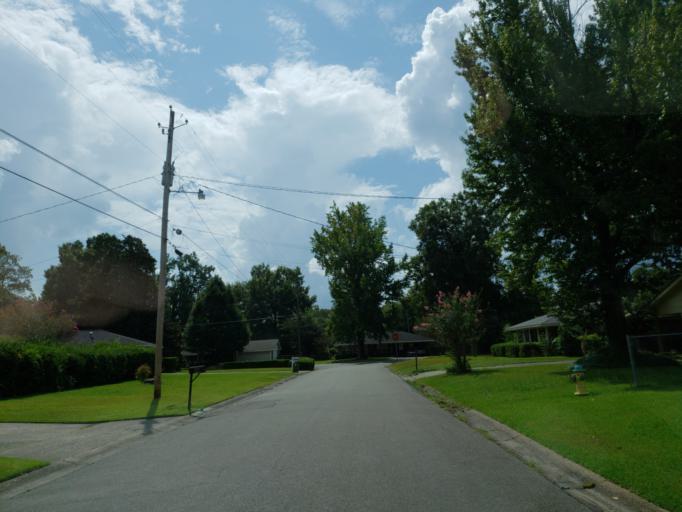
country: US
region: Mississippi
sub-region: Forrest County
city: Hattiesburg
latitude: 31.3292
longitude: -89.3231
